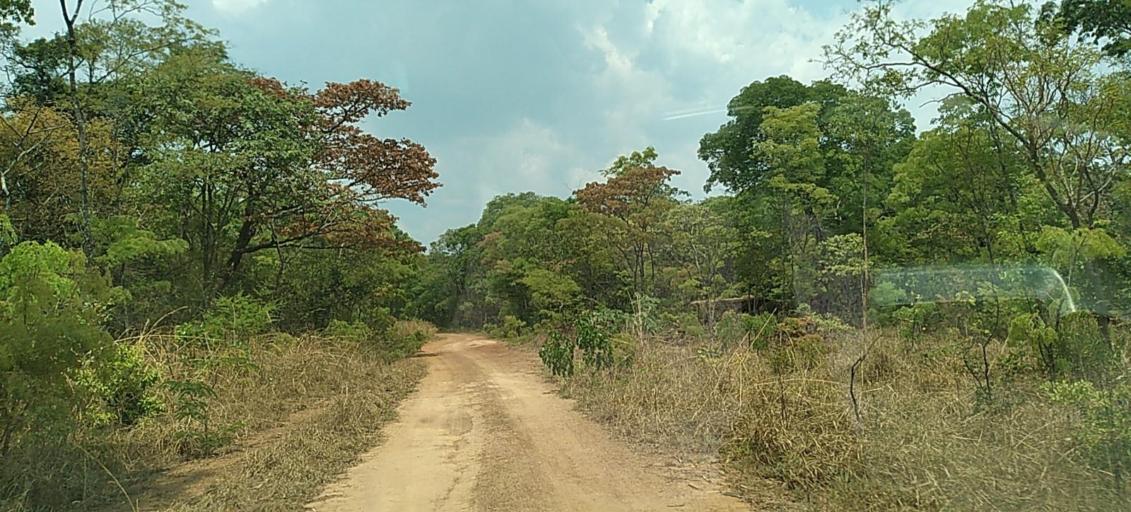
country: ZM
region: Copperbelt
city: Chingola
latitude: -12.7894
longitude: 27.6553
